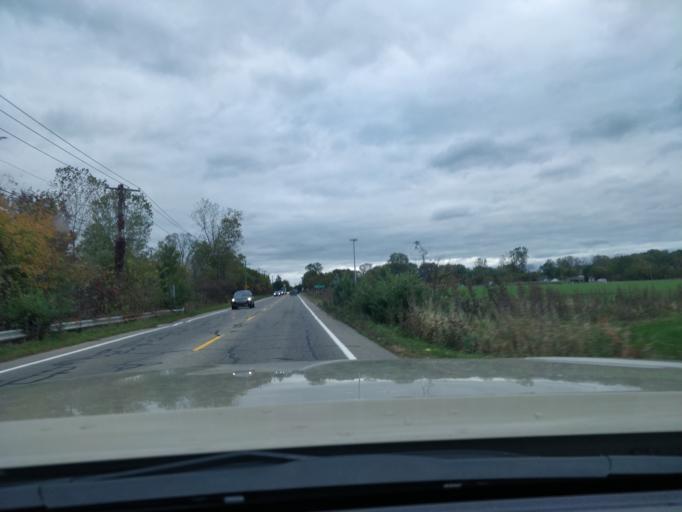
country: US
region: Michigan
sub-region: Wayne County
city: Romulus
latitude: 42.1809
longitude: -83.3297
